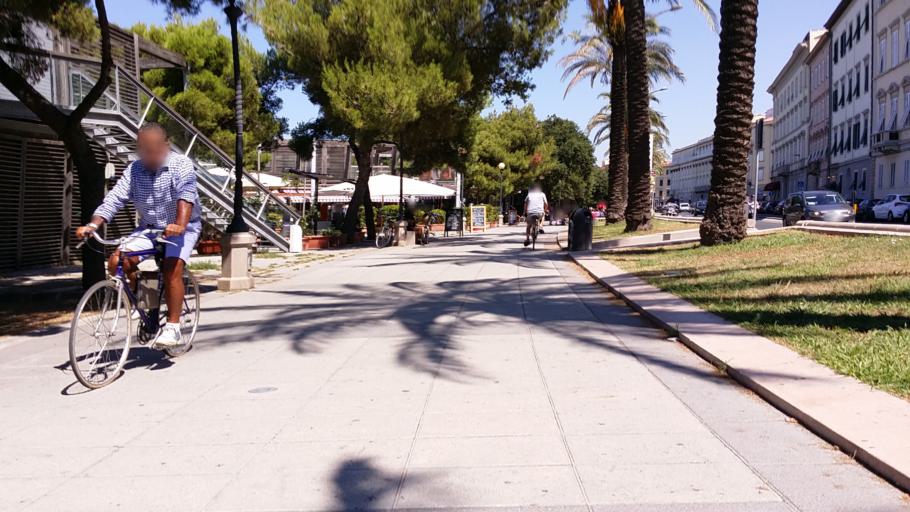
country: IT
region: Tuscany
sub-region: Provincia di Livorno
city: Livorno
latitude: 43.5356
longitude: 10.3012
